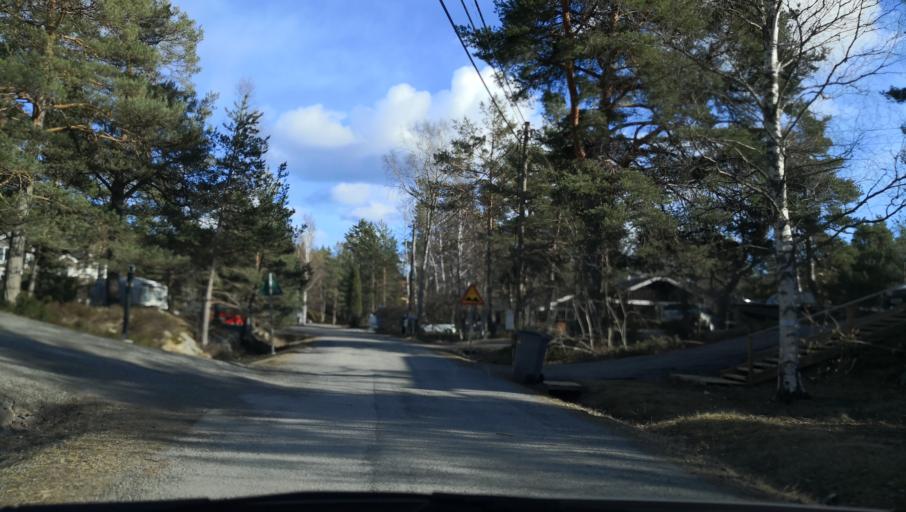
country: SE
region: Stockholm
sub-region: Varmdo Kommun
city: Hemmesta
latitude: 59.2438
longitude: 18.5152
